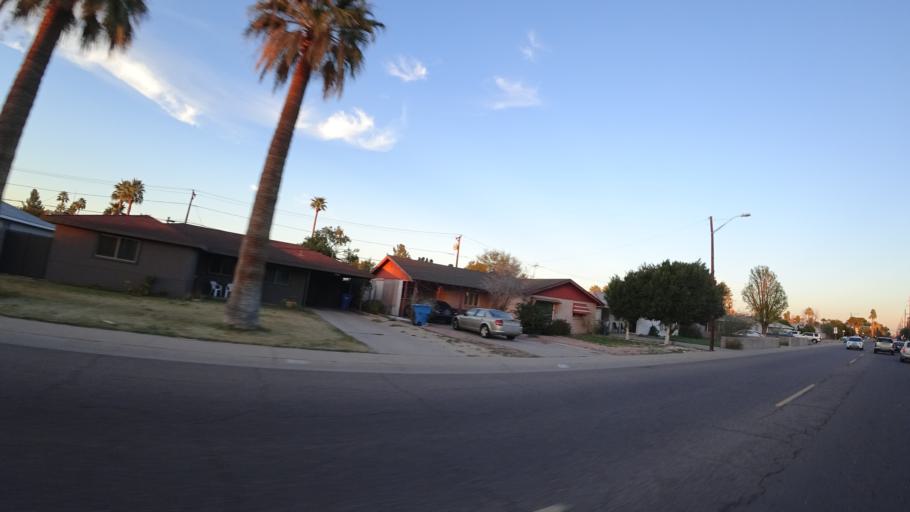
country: US
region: Arizona
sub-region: Maricopa County
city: Phoenix
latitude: 33.4731
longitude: -111.9983
